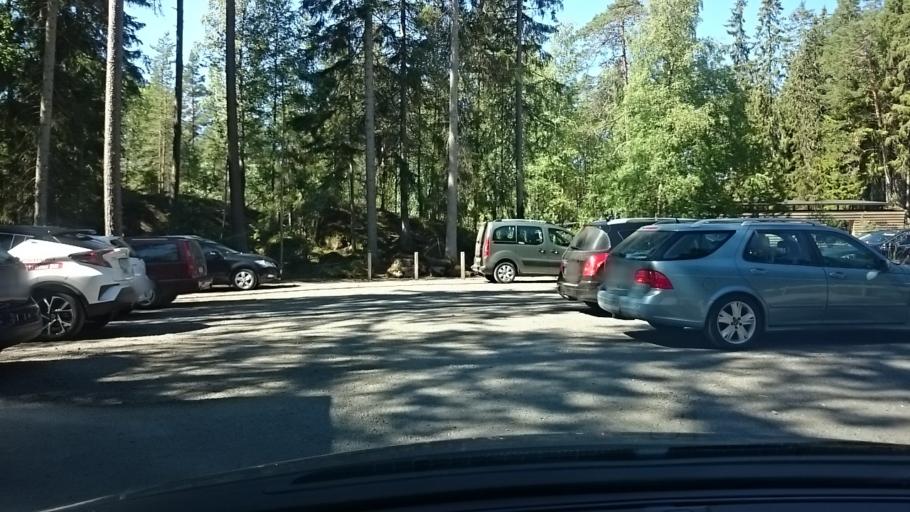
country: SE
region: Vaestra Goetaland
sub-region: Karlsborgs Kommun
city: Karlsborg
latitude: 58.7157
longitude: 14.5934
